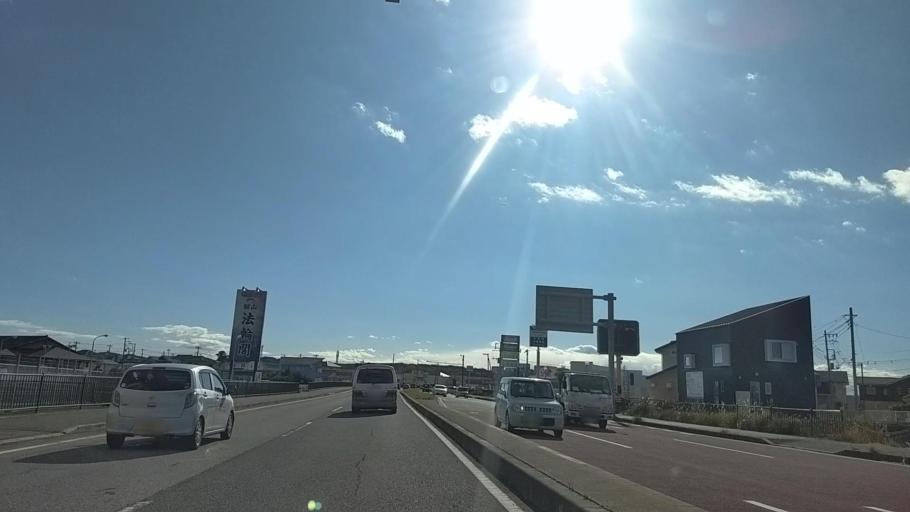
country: JP
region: Chiba
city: Tateyama
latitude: 34.9996
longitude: 139.8729
